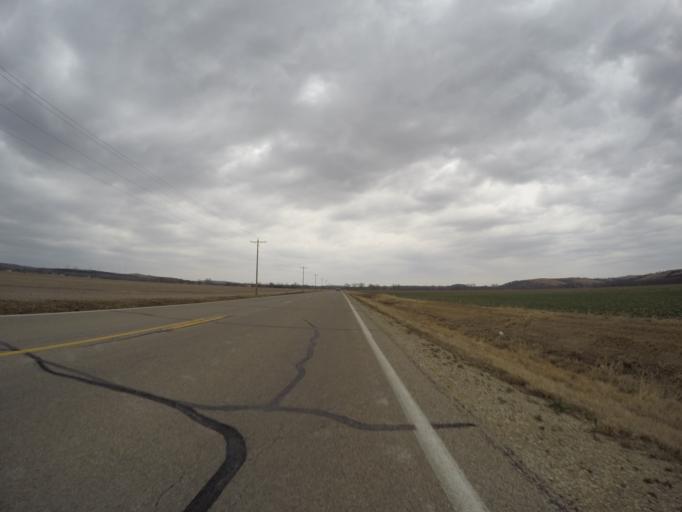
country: US
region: Kansas
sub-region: Riley County
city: Manhattan
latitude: 39.2295
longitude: -96.5643
